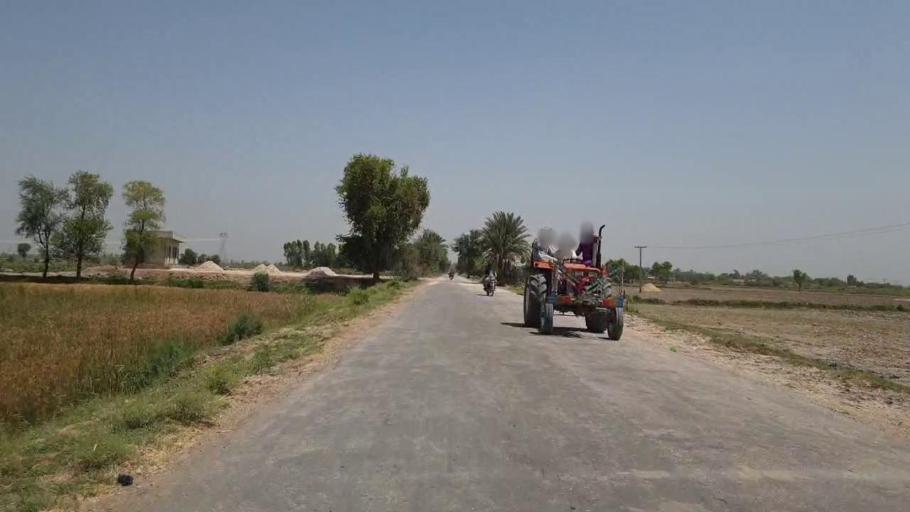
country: PK
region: Sindh
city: Adilpur
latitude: 27.8856
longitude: 69.2880
